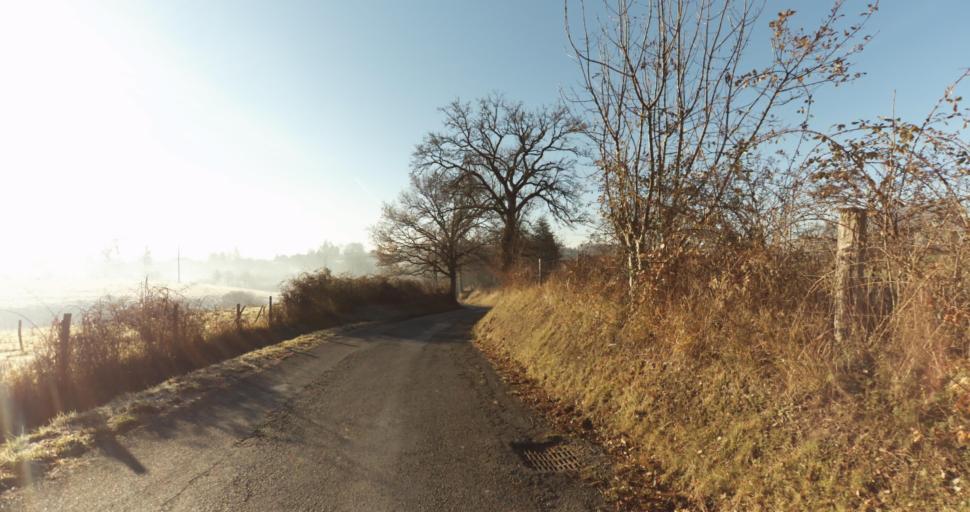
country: FR
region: Limousin
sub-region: Departement de la Haute-Vienne
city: Aixe-sur-Vienne
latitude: 45.8123
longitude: 1.1429
